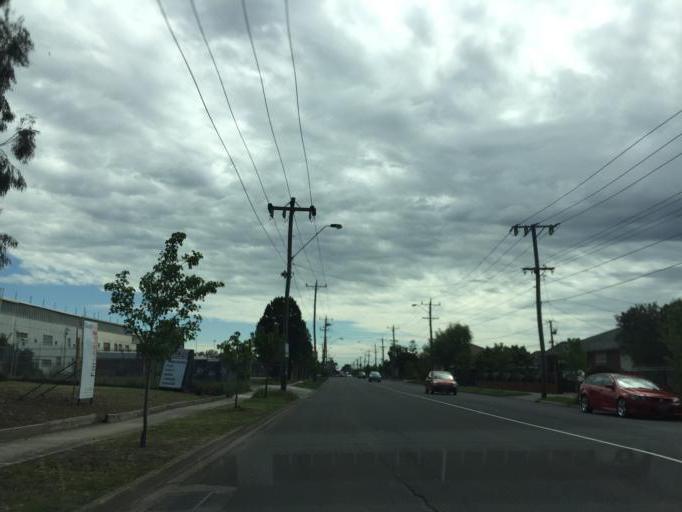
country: AU
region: Victoria
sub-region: Maribyrnong
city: Braybrook
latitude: -37.7905
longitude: 144.8637
